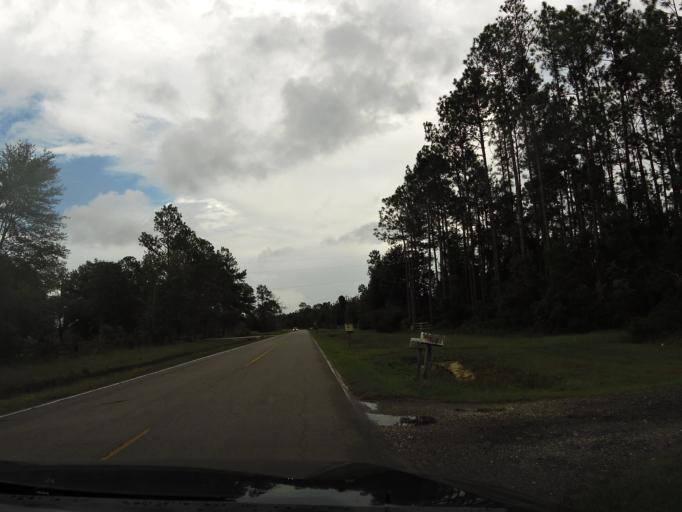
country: US
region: Florida
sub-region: Duval County
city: Baldwin
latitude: 30.4080
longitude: -82.0240
